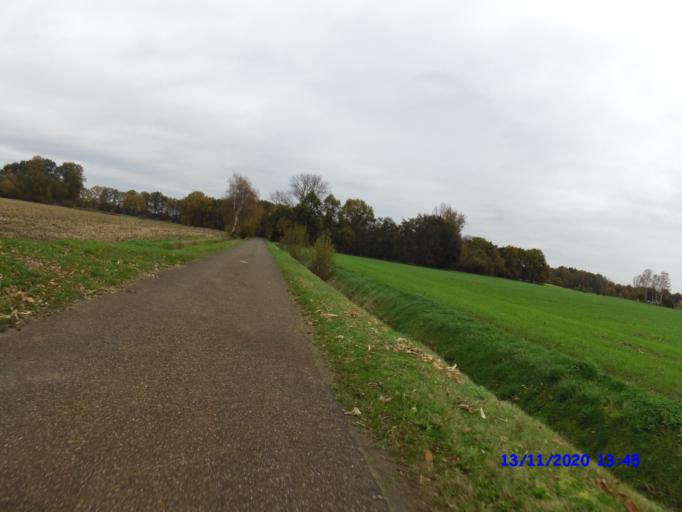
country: BE
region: Flanders
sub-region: Provincie Antwerpen
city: Kasterlee
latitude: 51.2649
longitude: 4.9865
